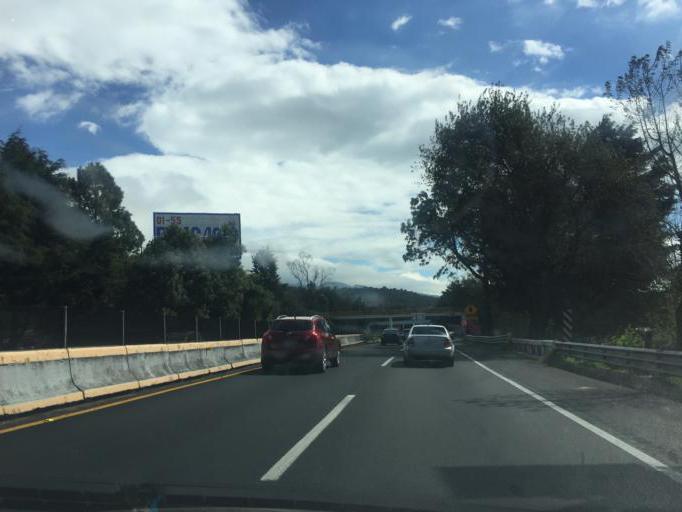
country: MX
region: Morelos
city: Tres Marias
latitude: 19.0320
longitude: -99.2083
